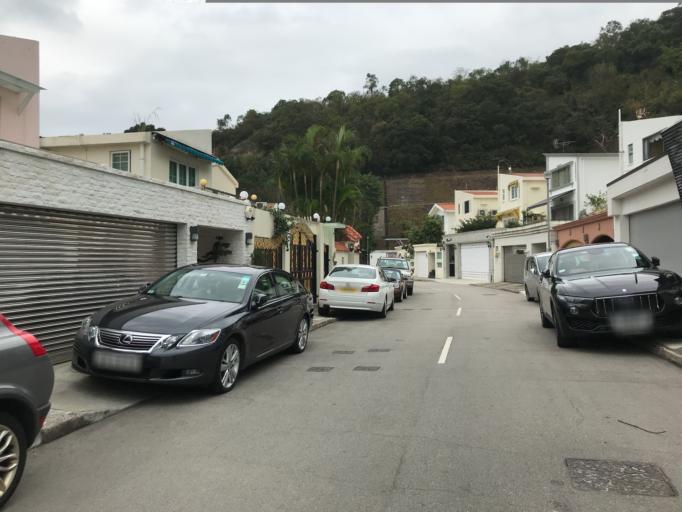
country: HK
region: Tai Po
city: Tai Po
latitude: 22.4642
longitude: 114.1610
